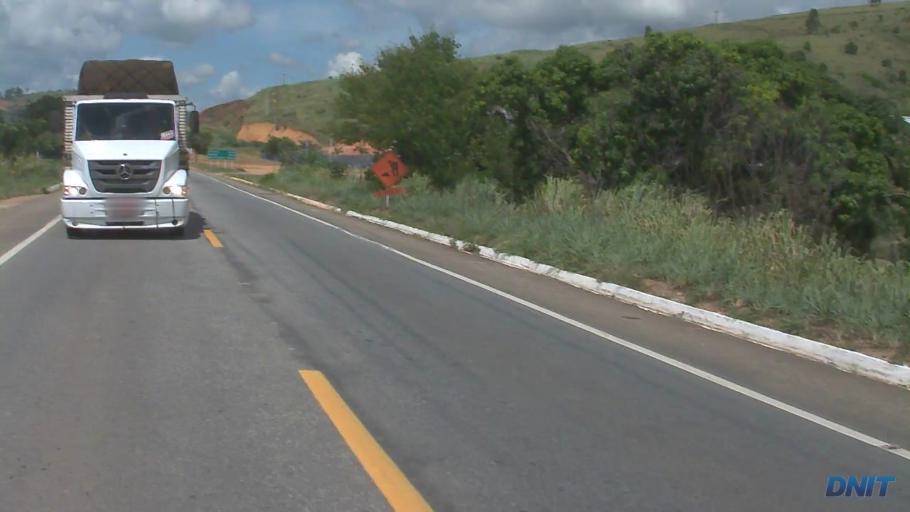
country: BR
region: Minas Gerais
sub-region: Governador Valadares
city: Governador Valadares
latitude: -18.9249
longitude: -42.0353
